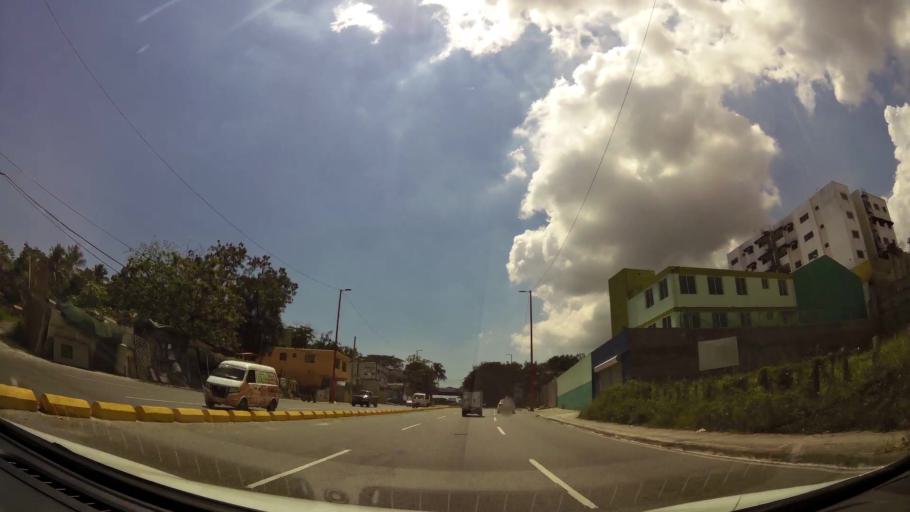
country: DO
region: Nacional
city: La Agustina
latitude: 18.5120
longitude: -69.9563
